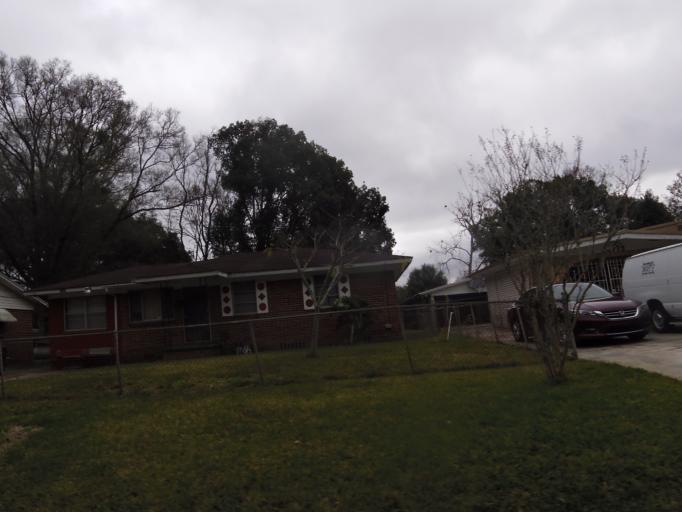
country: US
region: Florida
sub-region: Duval County
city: Jacksonville
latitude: 30.3724
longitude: -81.7094
